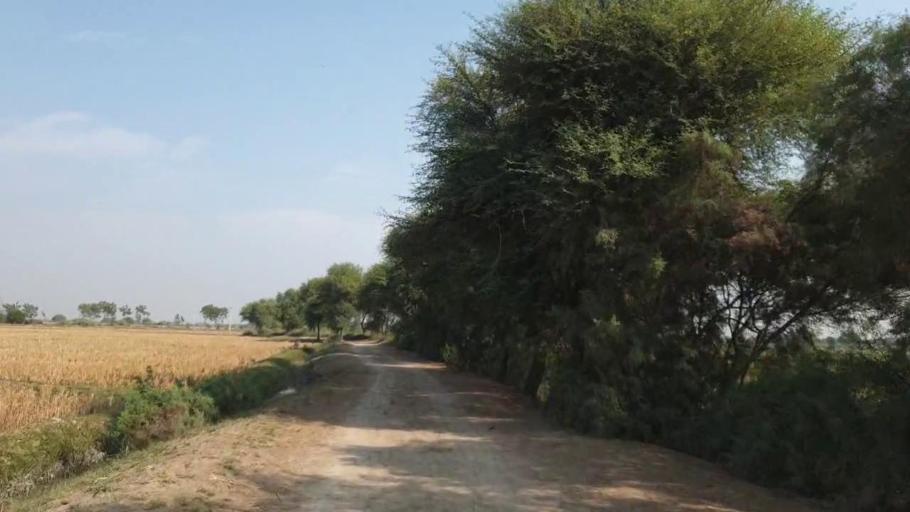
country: PK
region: Sindh
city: Tando Muhammad Khan
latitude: 25.0678
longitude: 68.4387
